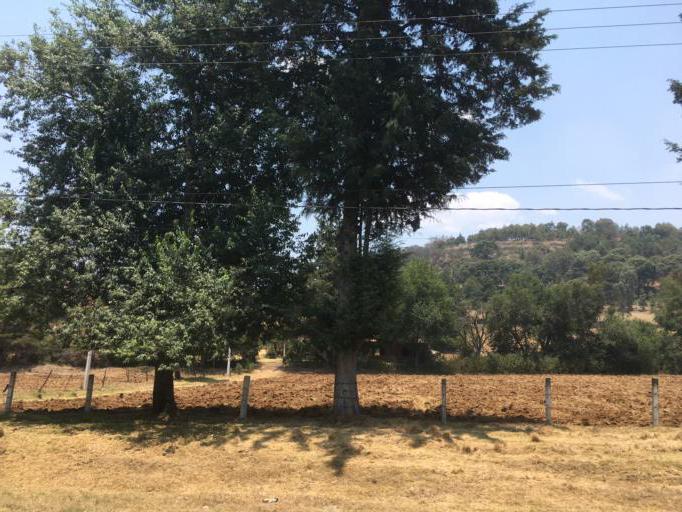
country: MX
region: Michoacan
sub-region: Morelia
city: Iratzio
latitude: 19.6252
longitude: -101.4632
